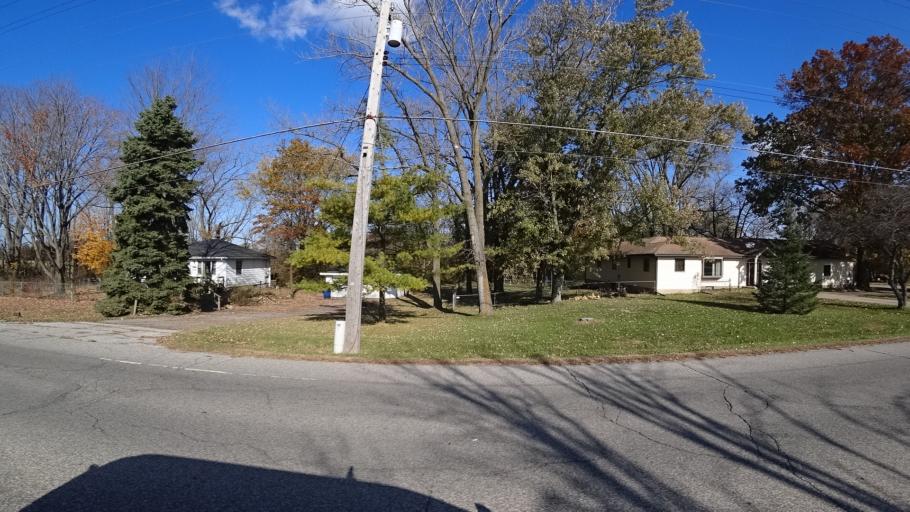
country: US
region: Indiana
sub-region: LaPorte County
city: Trail Creek
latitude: 41.6803
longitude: -86.8658
